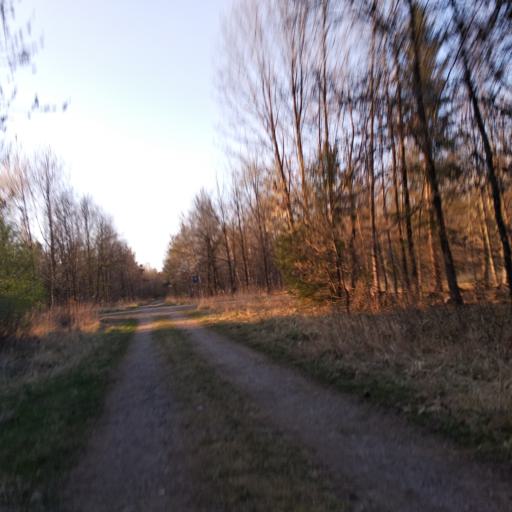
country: DE
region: Bavaria
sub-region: Upper Bavaria
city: Vaterstetten
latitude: 48.1101
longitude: 11.7494
